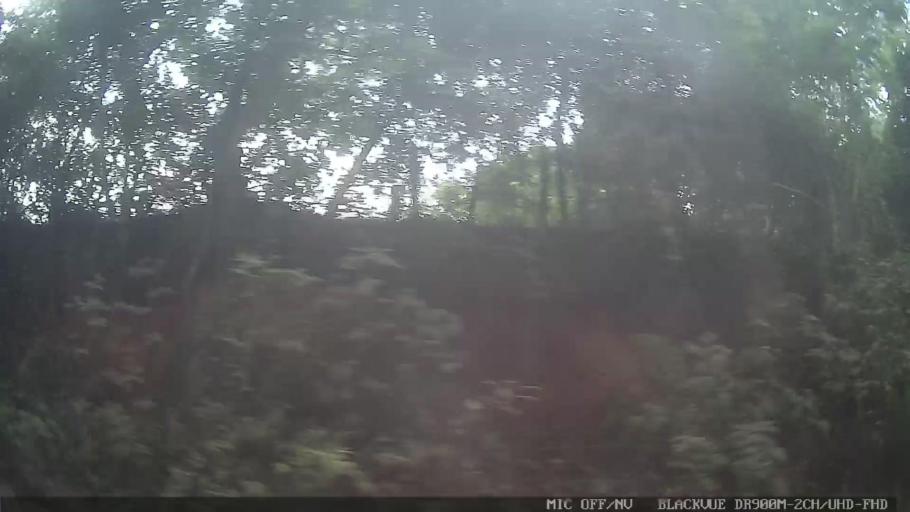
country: BR
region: Sao Paulo
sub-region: Bom Jesus Dos Perdoes
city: Bom Jesus dos Perdoes
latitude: -23.1364
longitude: -46.5094
